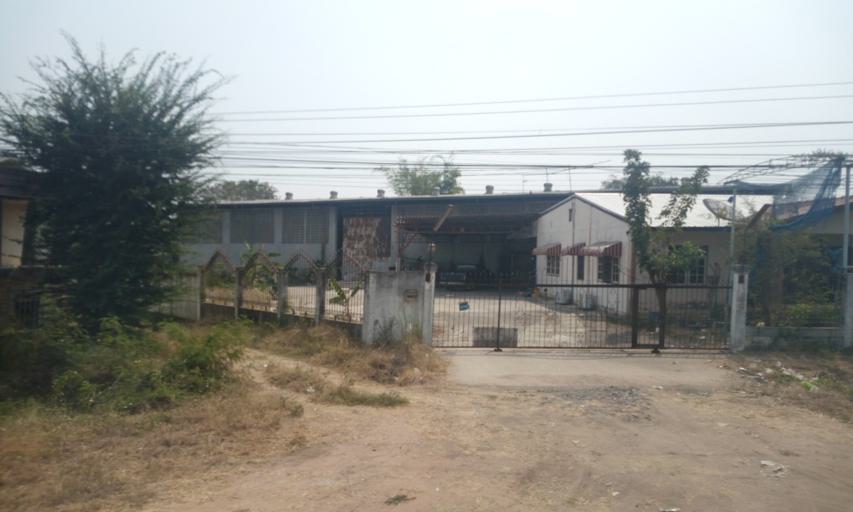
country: TH
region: Nakhon Ratchasima
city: Non Sung
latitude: 15.1442
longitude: 102.3211
